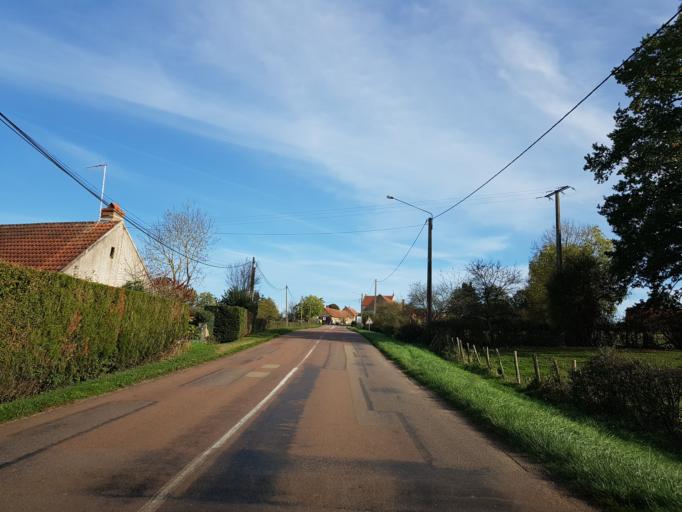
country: FR
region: Bourgogne
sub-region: Departement de la Cote-d'Or
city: Semur-en-Auxois
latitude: 47.5033
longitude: 4.2361
